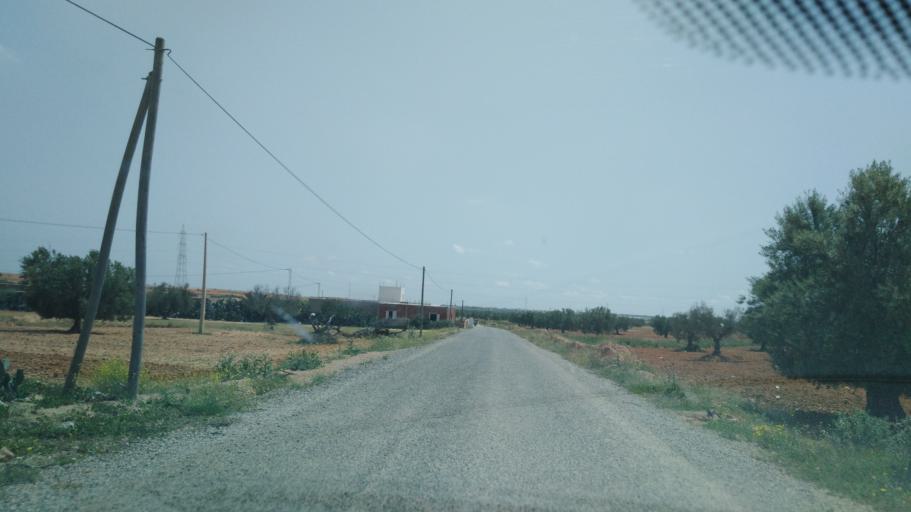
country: TN
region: Safaqis
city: Sfax
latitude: 34.7487
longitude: 10.5706
